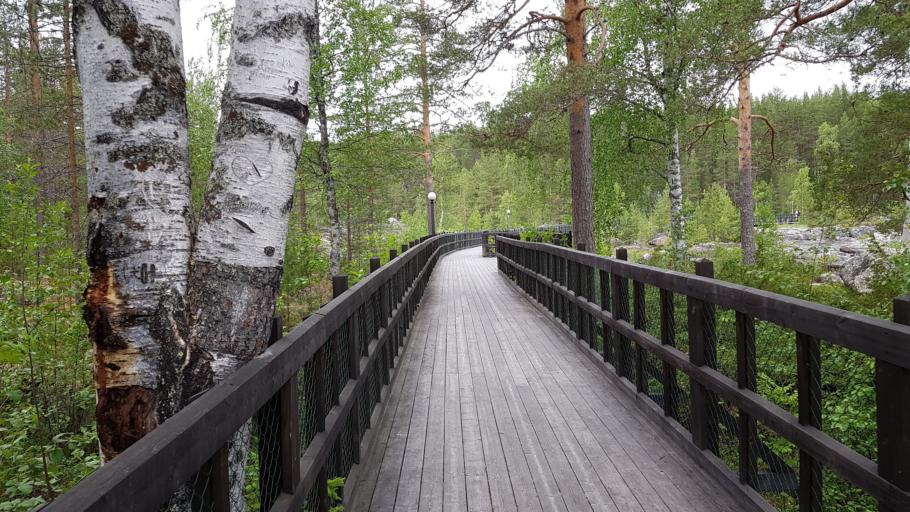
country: SE
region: Norrbotten
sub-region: Alvsbyns Kommun
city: AElvsbyn
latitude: 65.8503
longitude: 20.4049
